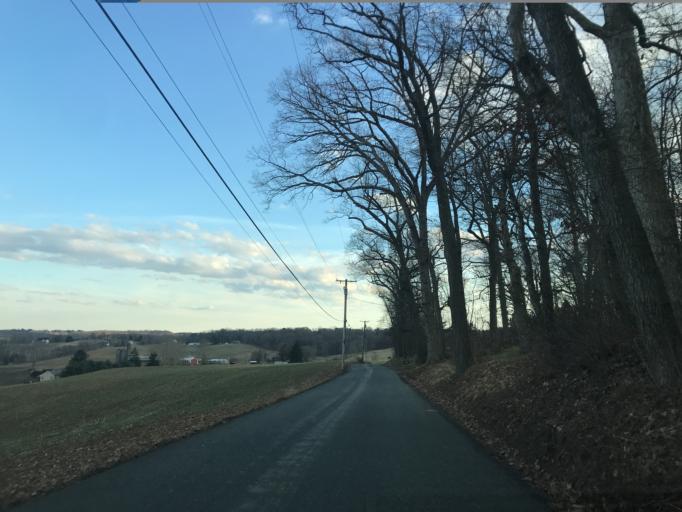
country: US
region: Maryland
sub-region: Harford County
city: Jarrettsville
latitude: 39.6160
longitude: -76.4202
